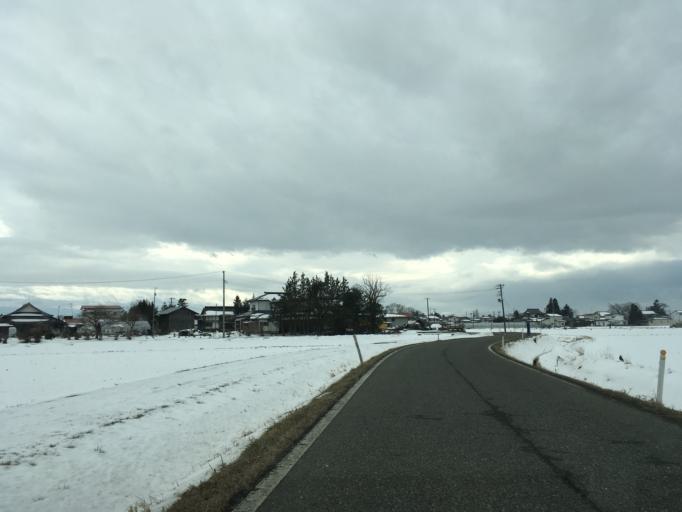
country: JP
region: Iwate
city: Ichinoseki
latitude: 38.7818
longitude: 141.1525
